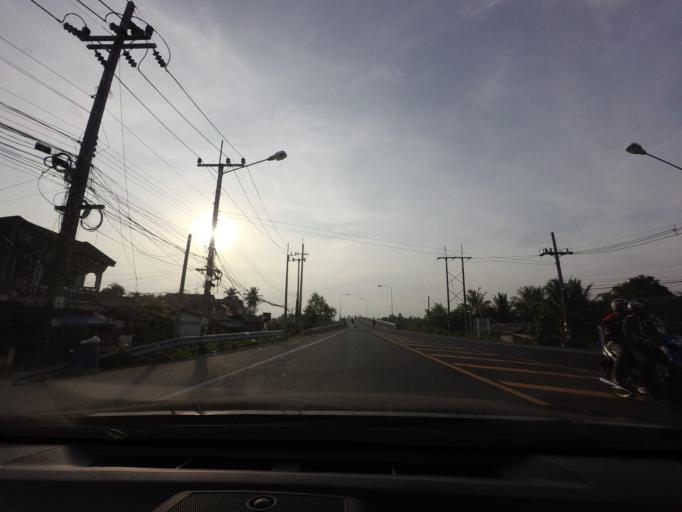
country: TH
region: Narathiwat
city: Narathiwat
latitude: 6.4174
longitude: 101.8429
